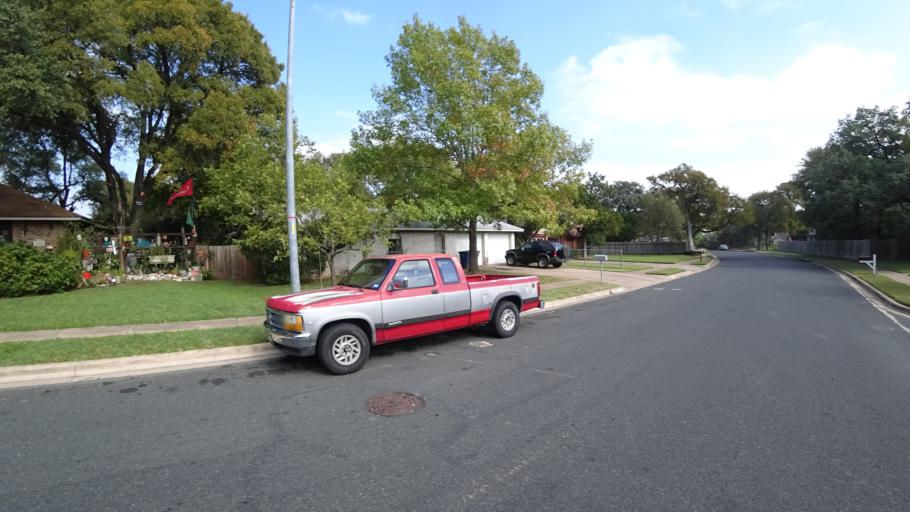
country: US
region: Texas
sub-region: Travis County
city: Shady Hollow
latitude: 30.2023
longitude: -97.8123
